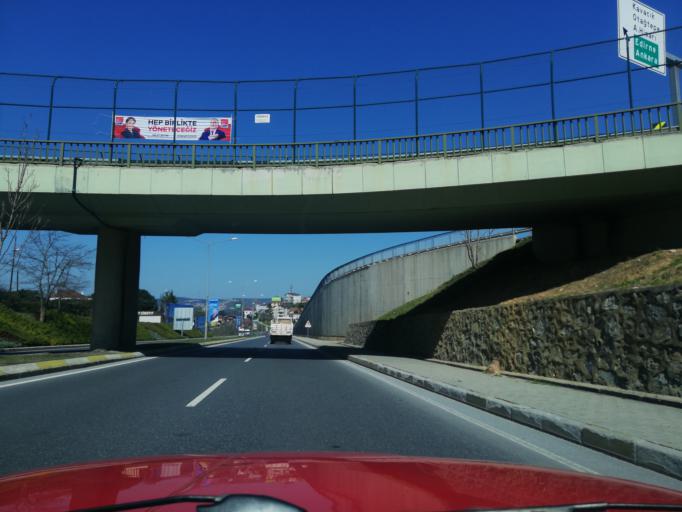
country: TR
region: Istanbul
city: Umraniye
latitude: 41.0995
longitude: 29.0974
